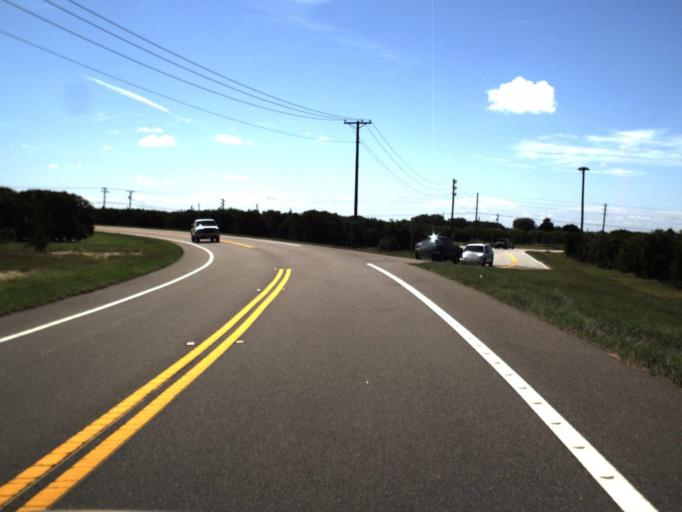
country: US
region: Florida
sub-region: Polk County
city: Crooked Lake Park
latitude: 27.8452
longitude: -81.5721
